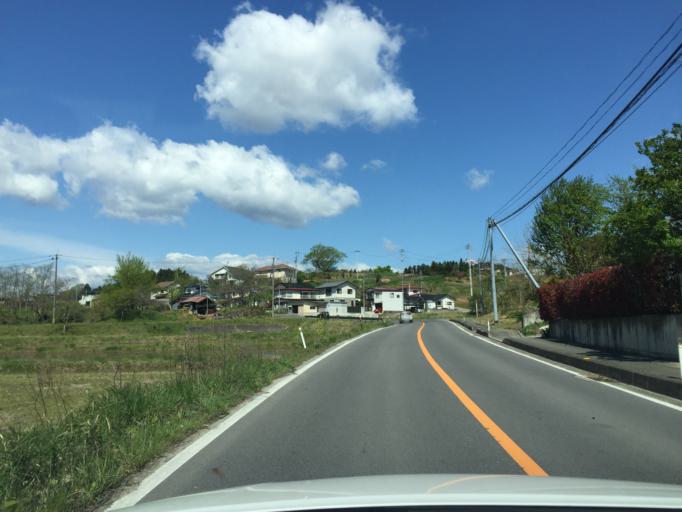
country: JP
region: Fukushima
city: Nihommatsu
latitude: 37.5722
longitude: 140.4721
